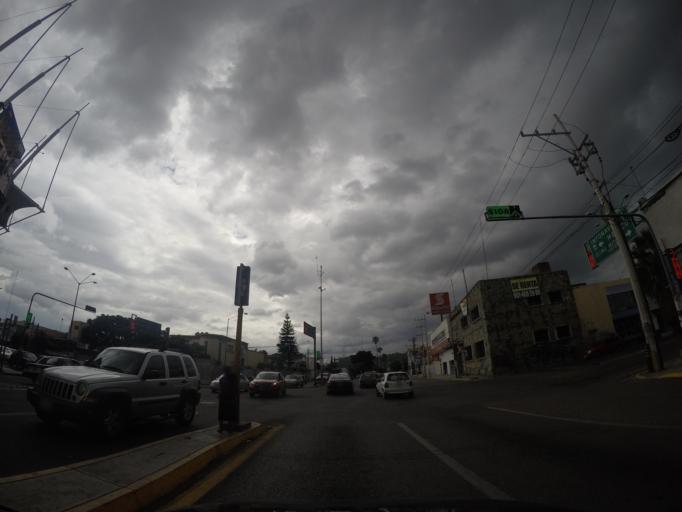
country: MX
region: Oaxaca
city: Oaxaca de Juarez
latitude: 17.0705
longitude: -96.7135
